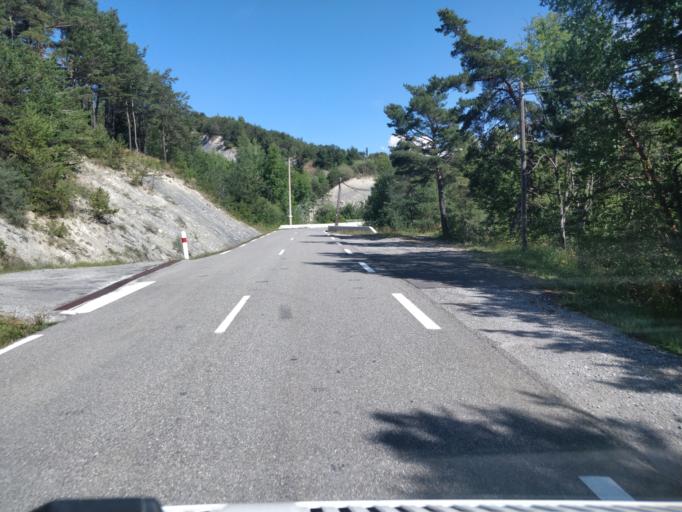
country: FR
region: Provence-Alpes-Cote d'Azur
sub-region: Departement des Alpes-de-Haute-Provence
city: Seyne-les-Alpes
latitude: 44.4055
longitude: 6.3340
